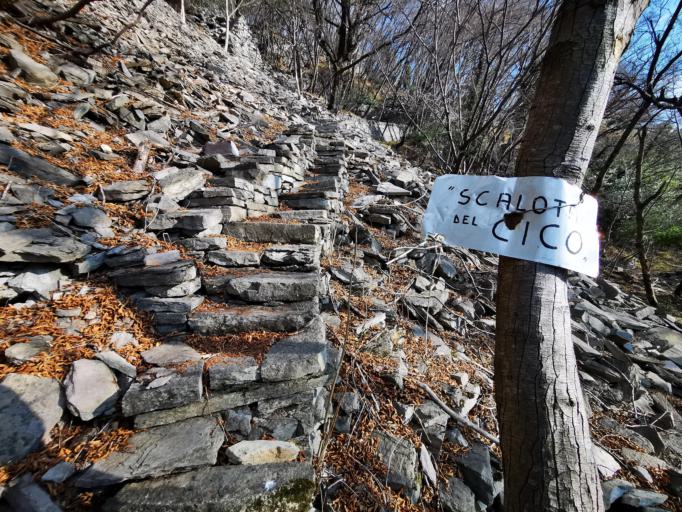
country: IT
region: Lombardy
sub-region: Provincia di Como
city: Carate Urio
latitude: 45.8738
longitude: 9.1203
